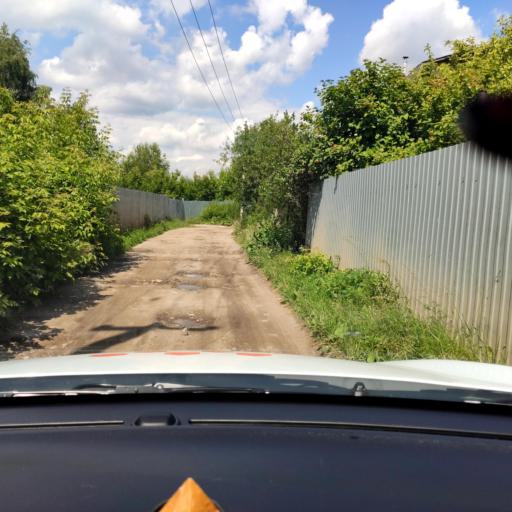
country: RU
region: Tatarstan
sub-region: Gorod Kazan'
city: Kazan
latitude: 55.8340
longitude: 49.2223
